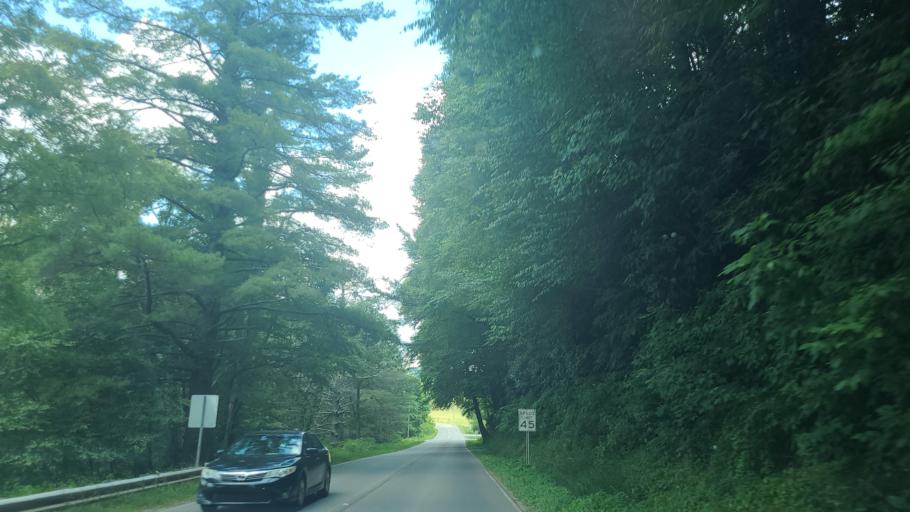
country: US
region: North Carolina
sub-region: Watauga County
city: Boone
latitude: 36.2337
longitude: -81.5520
